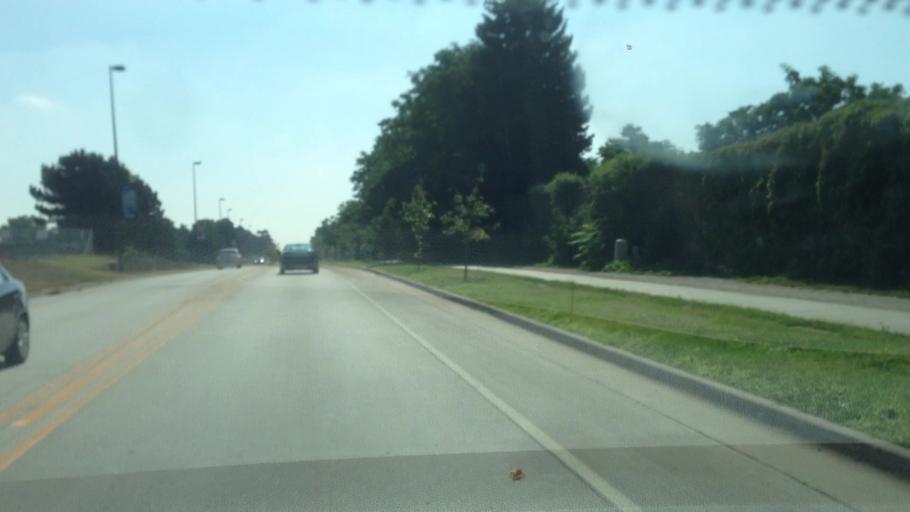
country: US
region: Colorado
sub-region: Denver County
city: Denver
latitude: 39.7512
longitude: -104.9534
